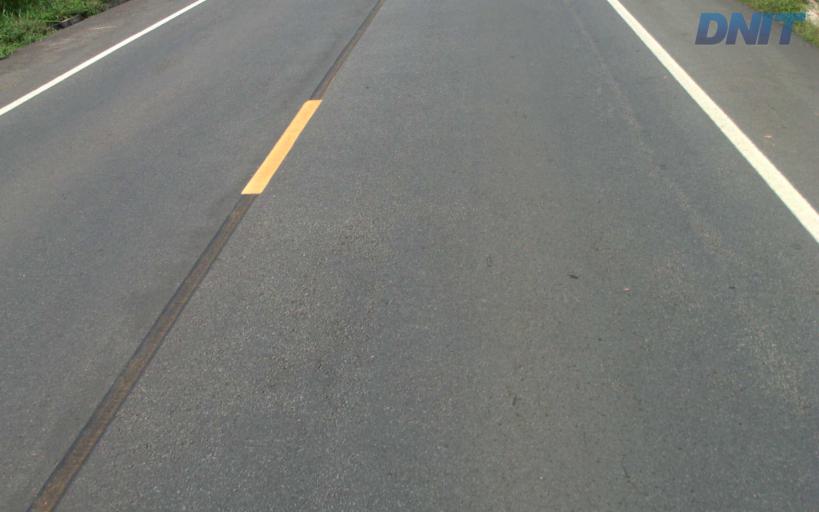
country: BR
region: Minas Gerais
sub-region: Belo Oriente
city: Belo Oriente
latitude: -19.2054
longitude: -42.2962
